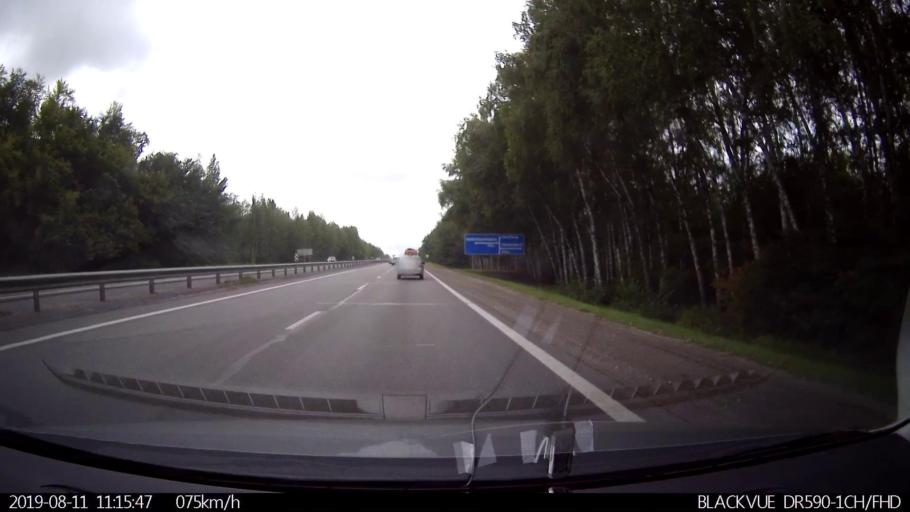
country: RU
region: Ulyanovsk
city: Novoul'yanovsk
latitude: 54.1998
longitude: 48.2875
